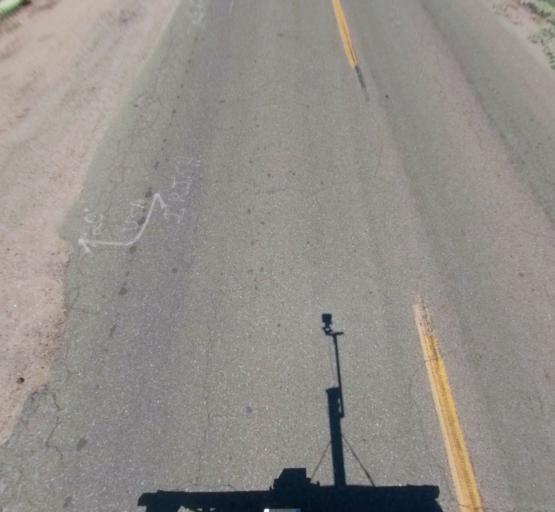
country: US
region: California
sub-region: Madera County
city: Fairmead
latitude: 37.0981
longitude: -120.1321
